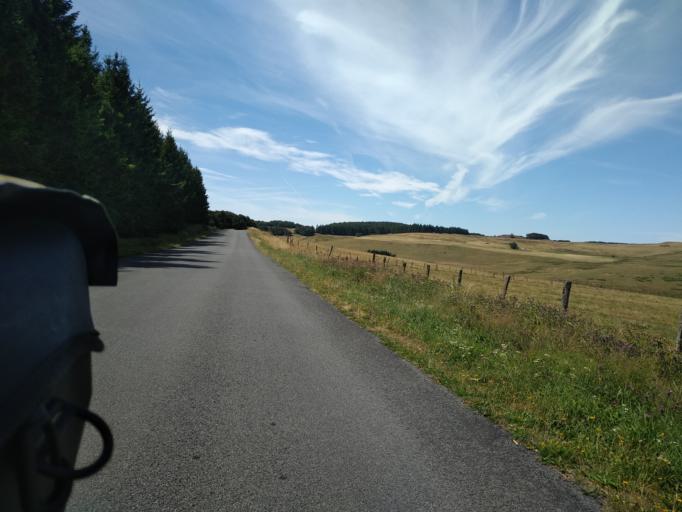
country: FR
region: Midi-Pyrenees
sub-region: Departement de l'Aveyron
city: Laguiole
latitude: 44.6658
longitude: 2.9606
